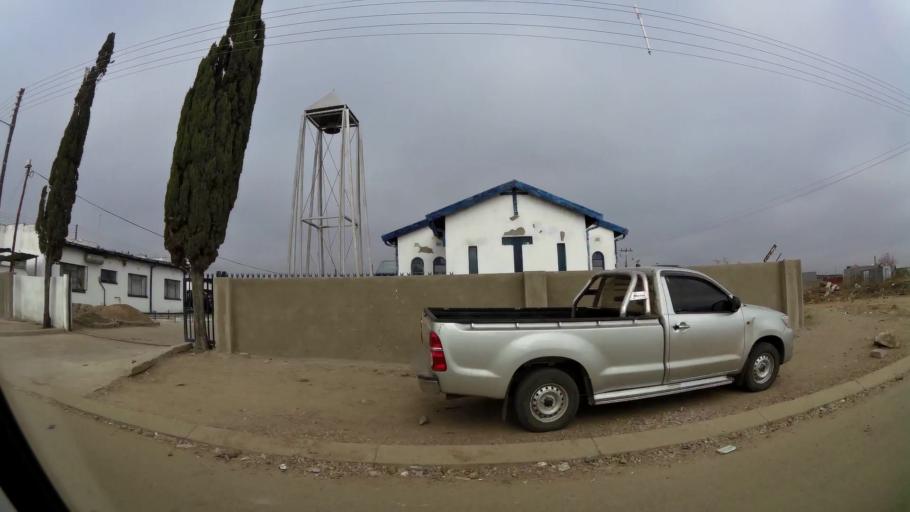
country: ZA
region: Limpopo
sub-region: Capricorn District Municipality
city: Polokwane
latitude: -23.8392
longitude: 29.3840
